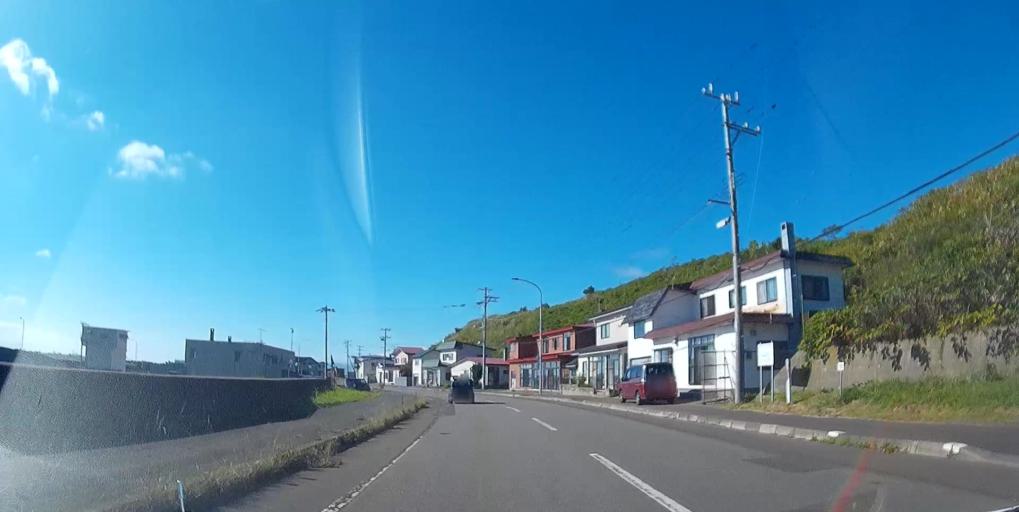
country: JP
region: Hokkaido
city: Kamiiso
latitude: 42.1380
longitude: 139.9204
